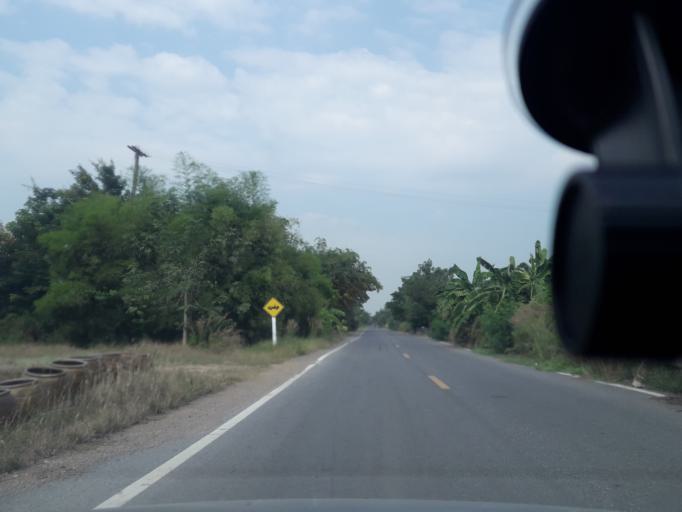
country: TH
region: Sara Buri
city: Nong Khae
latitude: 14.2301
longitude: 100.8914
